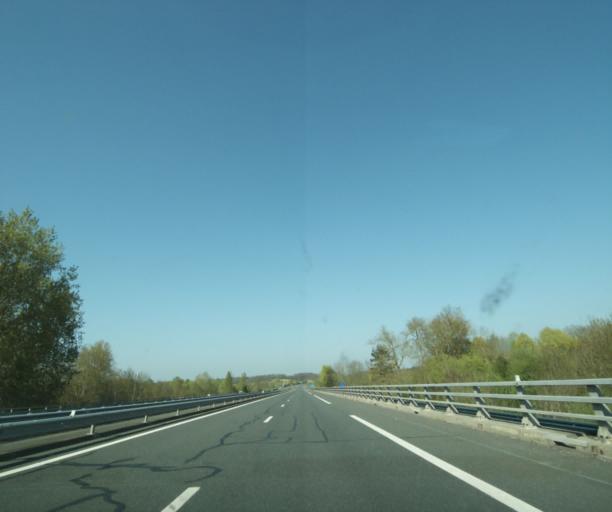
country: FR
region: Centre
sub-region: Departement du Loiret
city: Dordives
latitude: 48.1527
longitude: 2.7523
